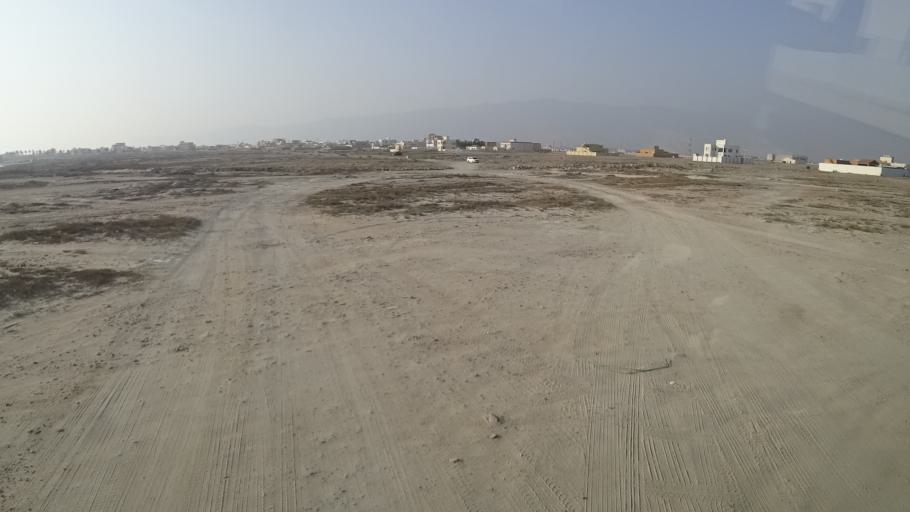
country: OM
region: Zufar
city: Salalah
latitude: 16.9735
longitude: 54.7008
